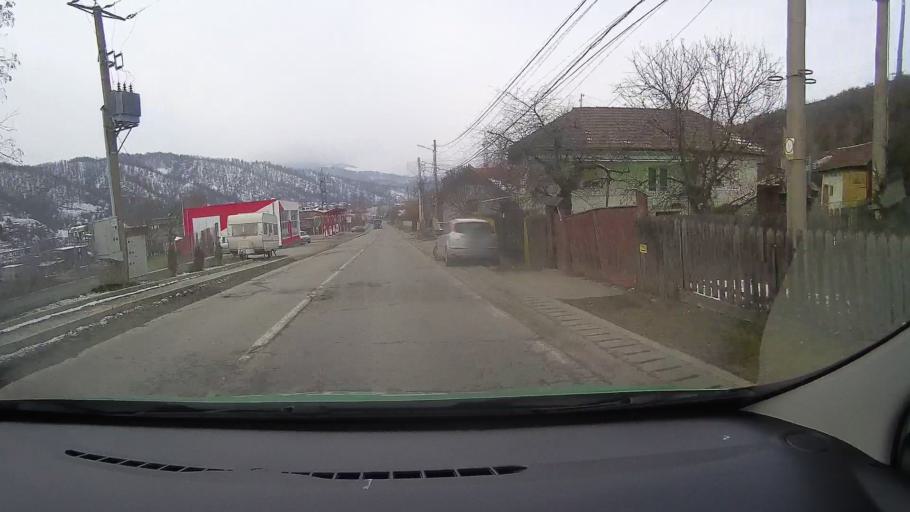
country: RO
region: Alba
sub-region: Oras Zlatna
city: Zlatna
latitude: 46.1070
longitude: 23.2369
